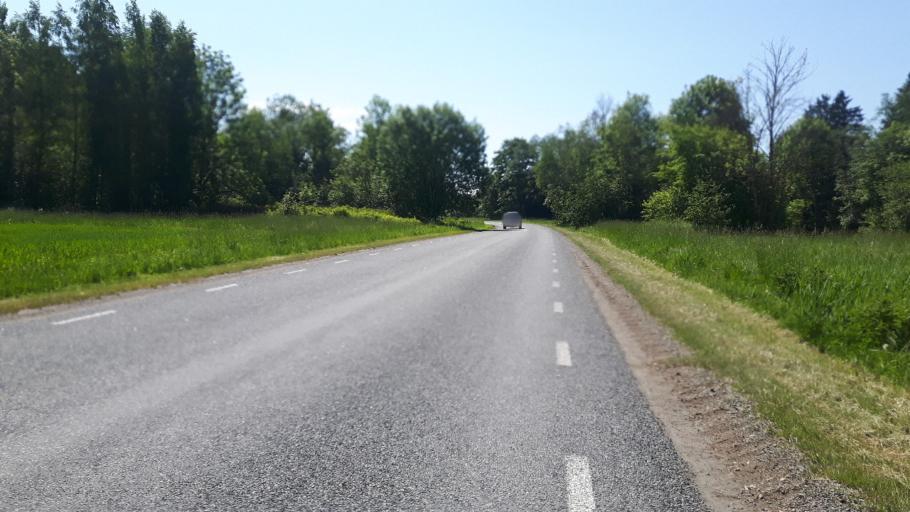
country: EE
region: Paernumaa
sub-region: Vaendra vald (alev)
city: Vandra
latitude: 58.5994
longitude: 25.0219
